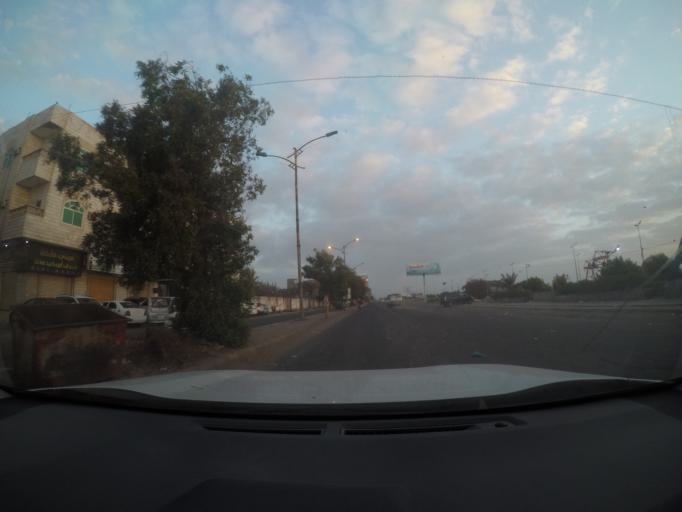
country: YE
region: Aden
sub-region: Khur Maksar
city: Khawr Maksar
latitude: 12.8434
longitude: 45.0524
